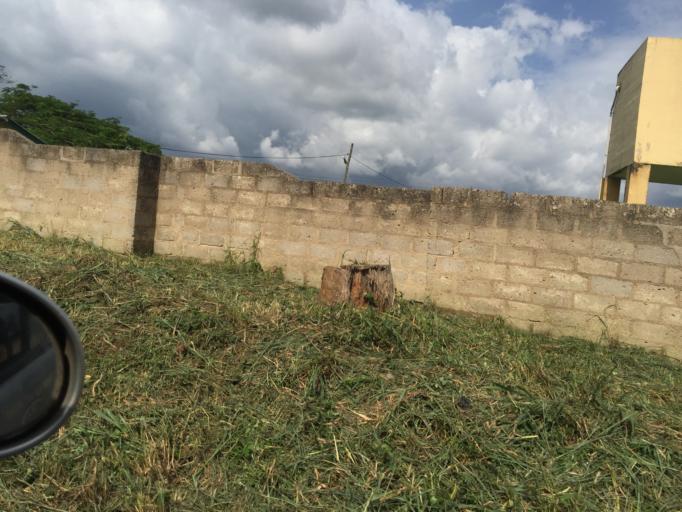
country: GH
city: Mpraeso
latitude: 6.6016
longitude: -0.7398
